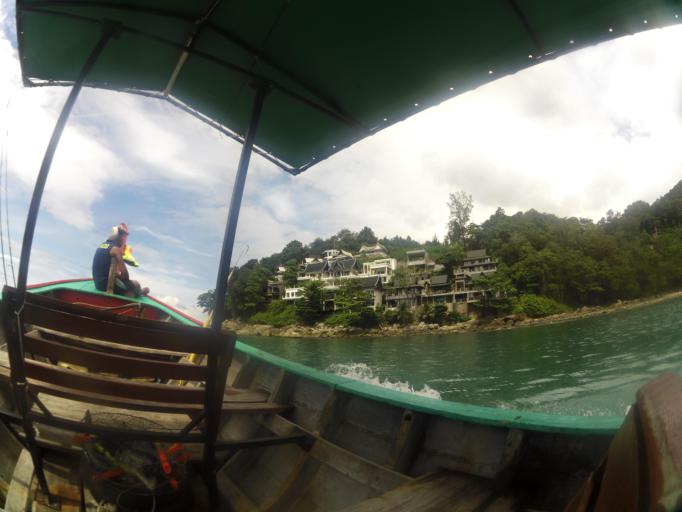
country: TH
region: Phuket
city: Patong
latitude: 7.9633
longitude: 98.2797
